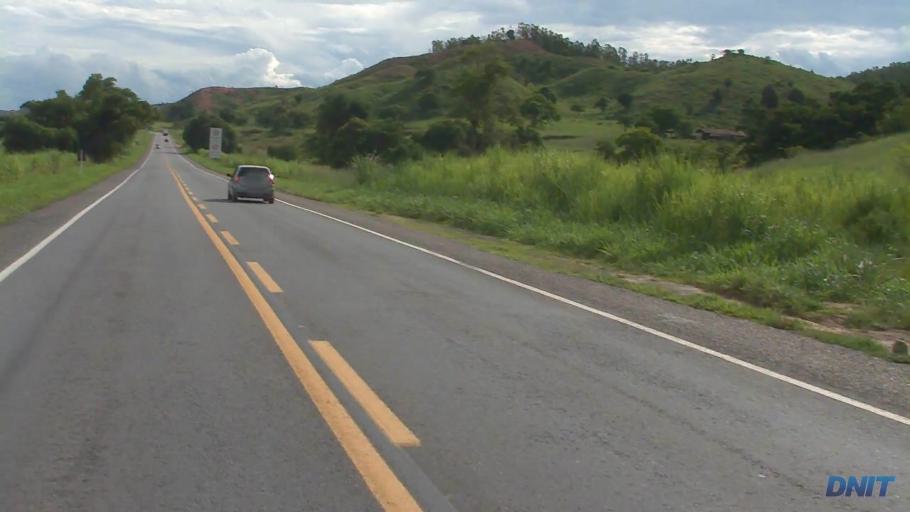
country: BR
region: Minas Gerais
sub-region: Belo Oriente
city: Belo Oriente
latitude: -19.1872
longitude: -42.2673
